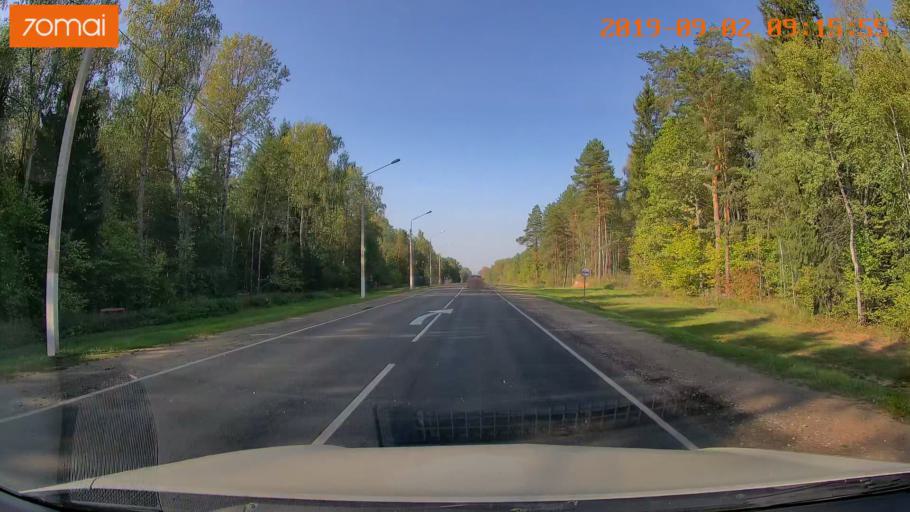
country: RU
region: Kaluga
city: Nikola-Lenivets
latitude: 54.8359
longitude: 35.4851
